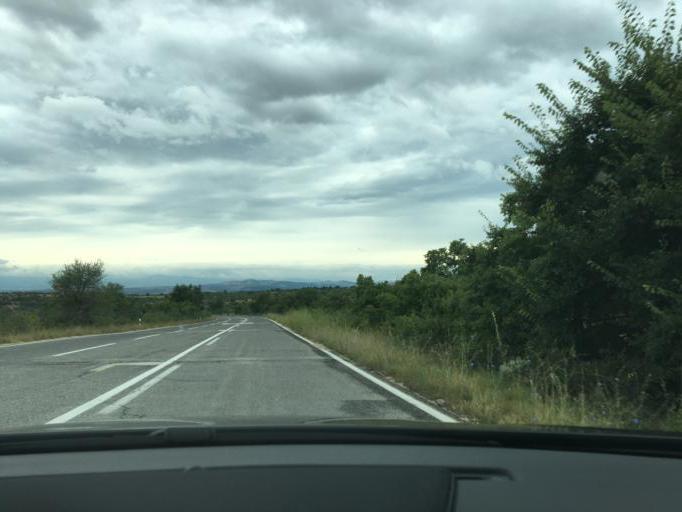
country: MK
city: Klechovce
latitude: 42.1501
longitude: 21.9630
